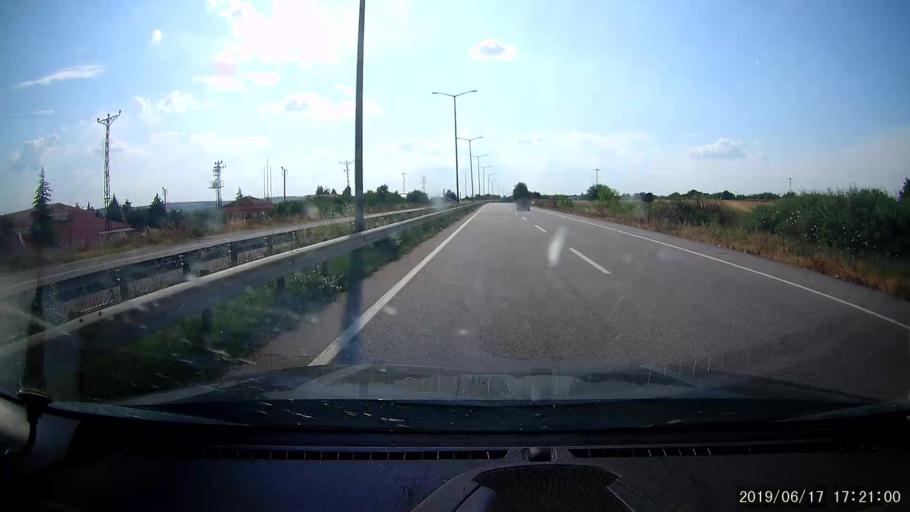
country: GR
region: East Macedonia and Thrace
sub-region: Nomos Evrou
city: Rizia
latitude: 41.7043
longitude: 26.4027
